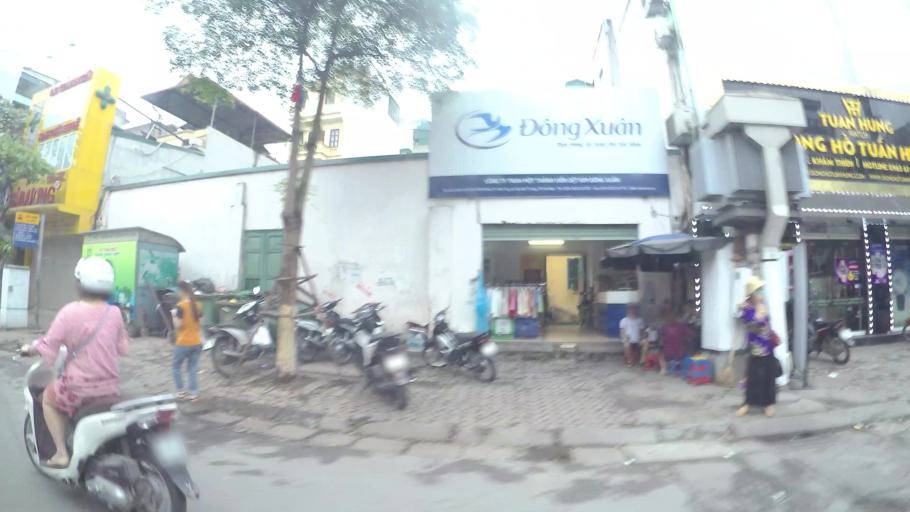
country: VN
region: Ha Noi
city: Dong Da
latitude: 21.0194
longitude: 105.8331
